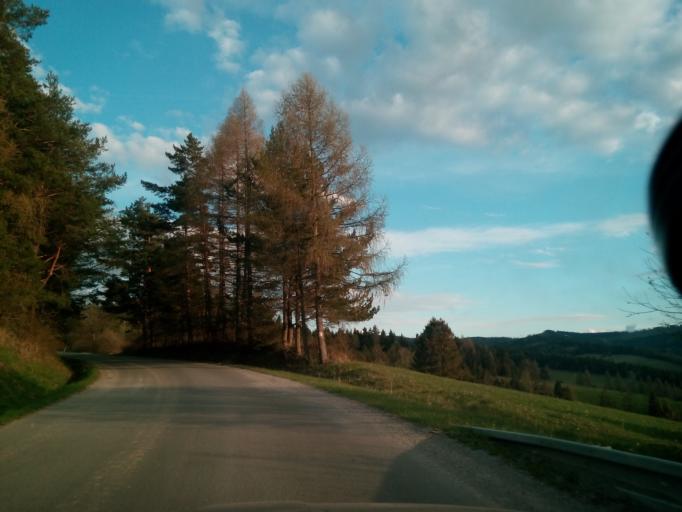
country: PL
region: Lesser Poland Voivodeship
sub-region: Powiat nowotarski
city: Niedzica
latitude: 49.3331
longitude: 20.3114
